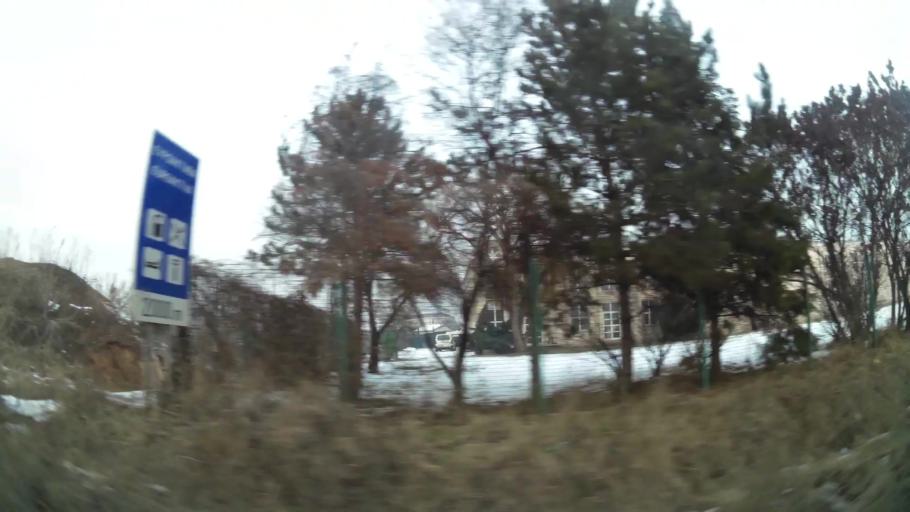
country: MK
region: Suto Orizari
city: Suto Orizare
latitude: 42.0333
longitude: 21.4024
